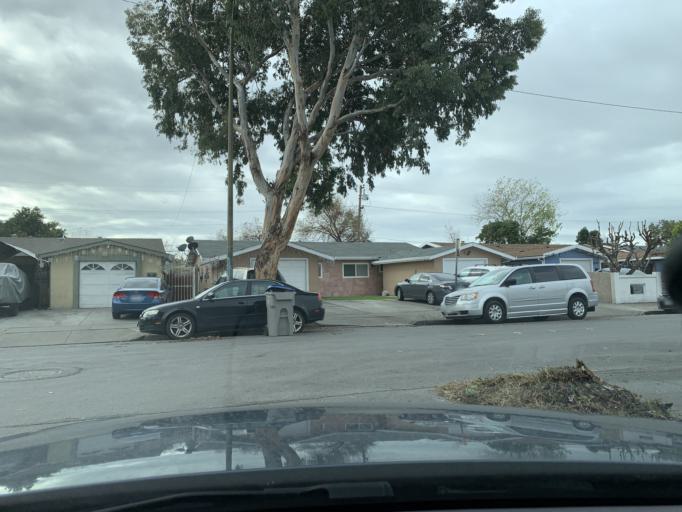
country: US
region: California
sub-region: Santa Clara County
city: Alum Rock
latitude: 37.3524
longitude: -121.8403
